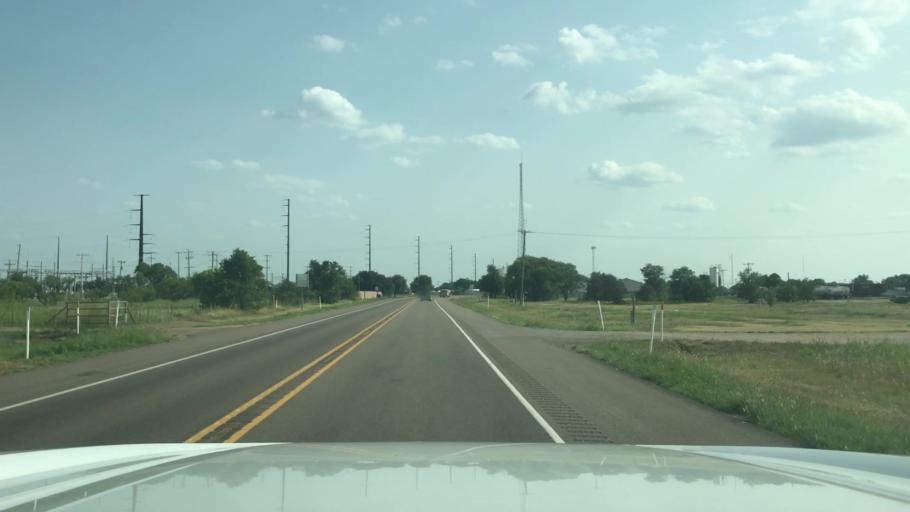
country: US
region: Texas
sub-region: Hartley County
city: Channing
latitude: 35.6915
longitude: -102.3283
